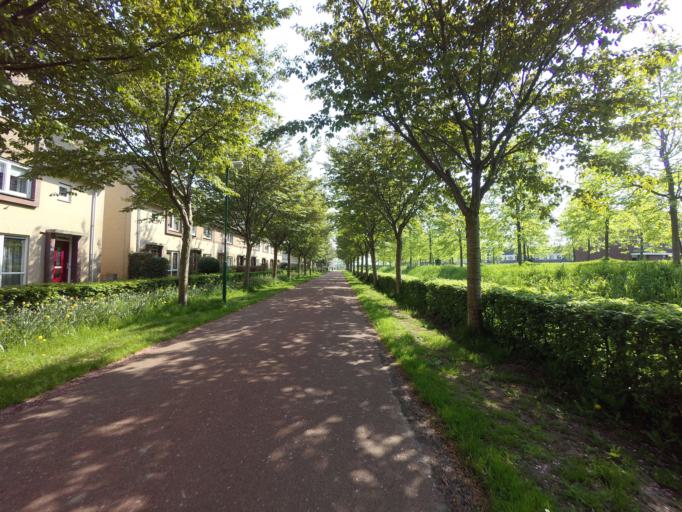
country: NL
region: Utrecht
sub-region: Gemeente Houten
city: Houten
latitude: 52.0135
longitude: 5.1884
